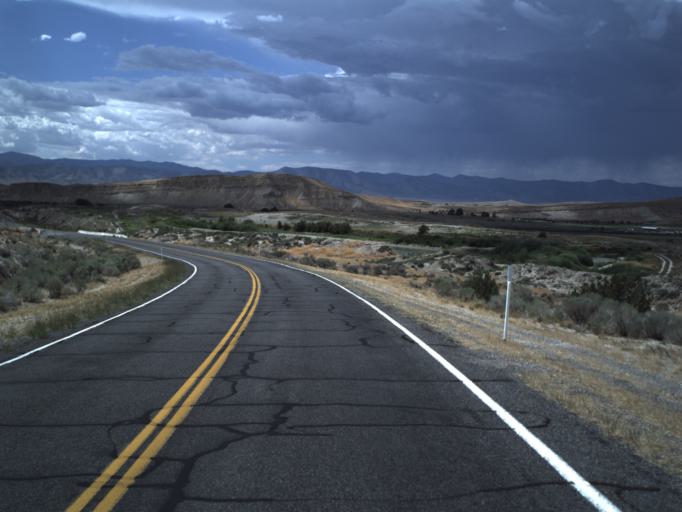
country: US
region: Utah
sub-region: Sanpete County
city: Gunnison
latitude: 39.1469
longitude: -111.7389
